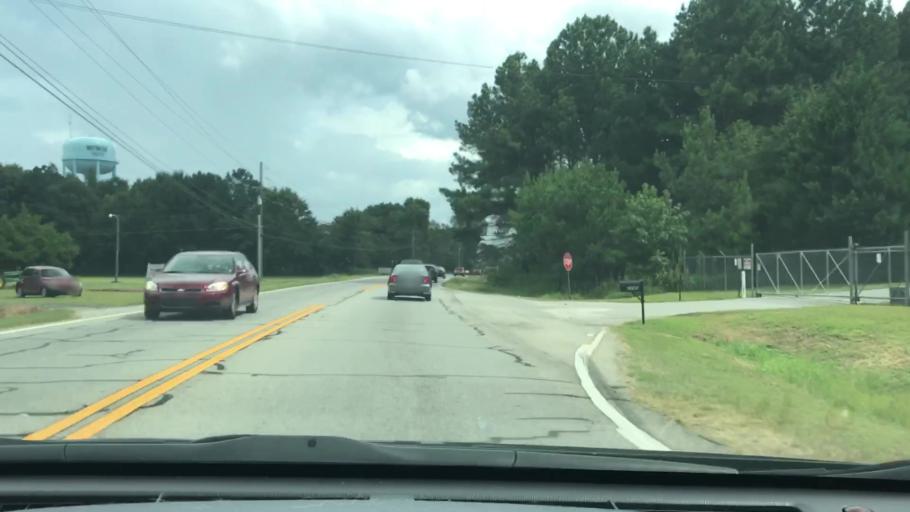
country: US
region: Georgia
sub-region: Walton County
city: Walnut Grove
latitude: 33.7906
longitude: -83.8591
